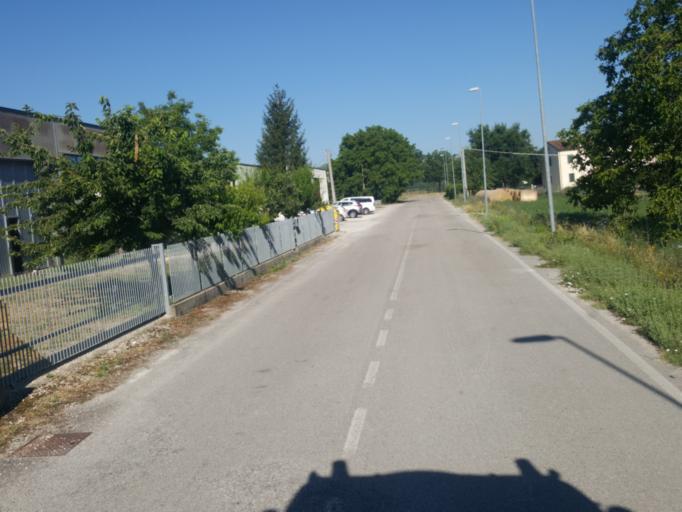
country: IT
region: The Marches
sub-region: Provincia di Pesaro e Urbino
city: Montecalvo in Foglia
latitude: 43.7858
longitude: 12.6324
